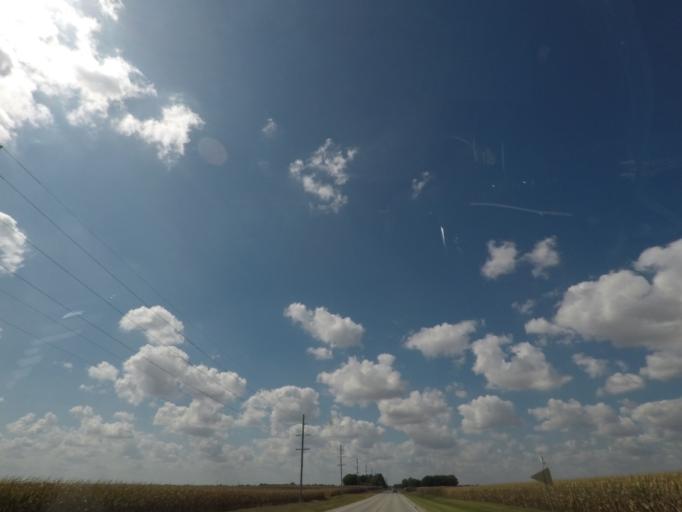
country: US
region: Iowa
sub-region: Story County
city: Nevada
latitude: 42.0227
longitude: -93.4100
